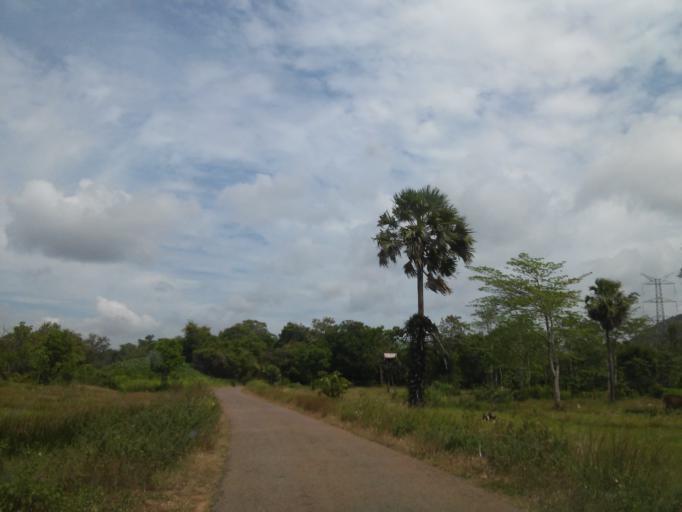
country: LK
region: Central
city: Sigiriya
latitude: 8.0884
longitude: 80.6771
